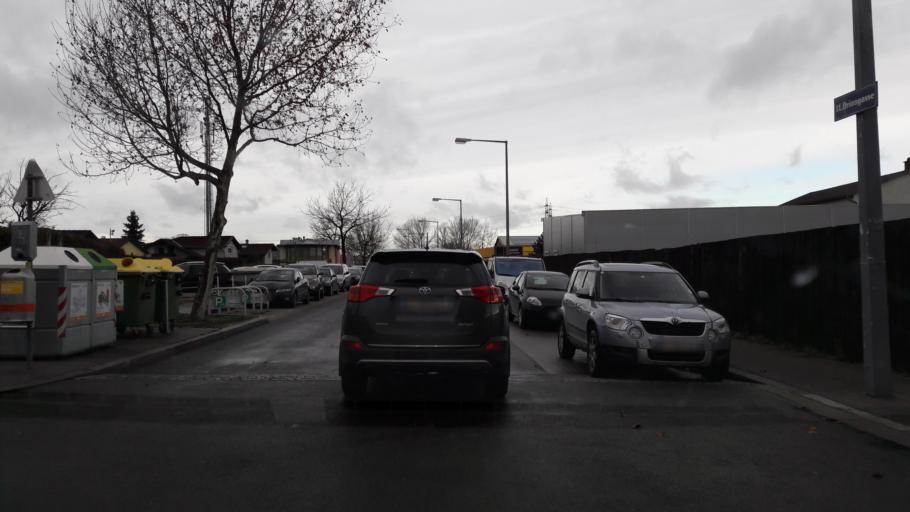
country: AT
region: Lower Austria
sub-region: Politischer Bezirk Wien-Umgebung
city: Schwechat
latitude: 48.1738
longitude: 16.4385
